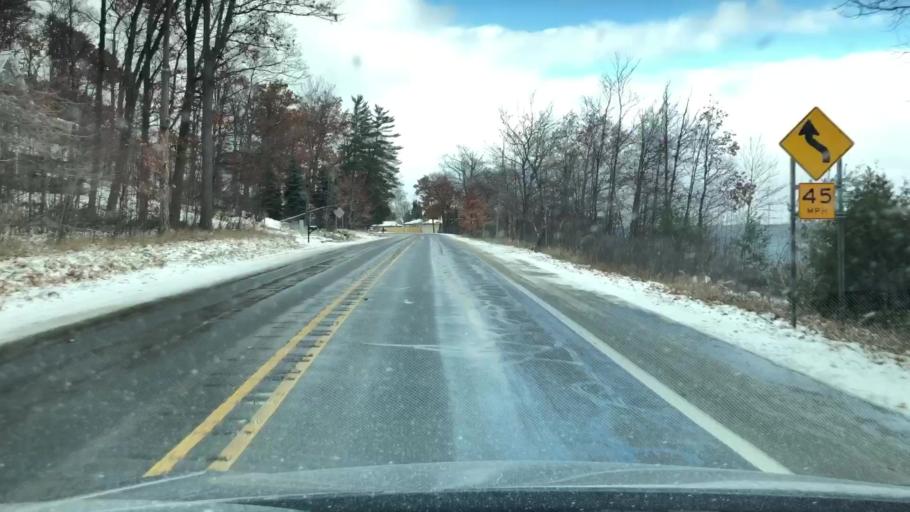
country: US
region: Michigan
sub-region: Grand Traverse County
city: Traverse City
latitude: 44.8234
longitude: -85.5507
